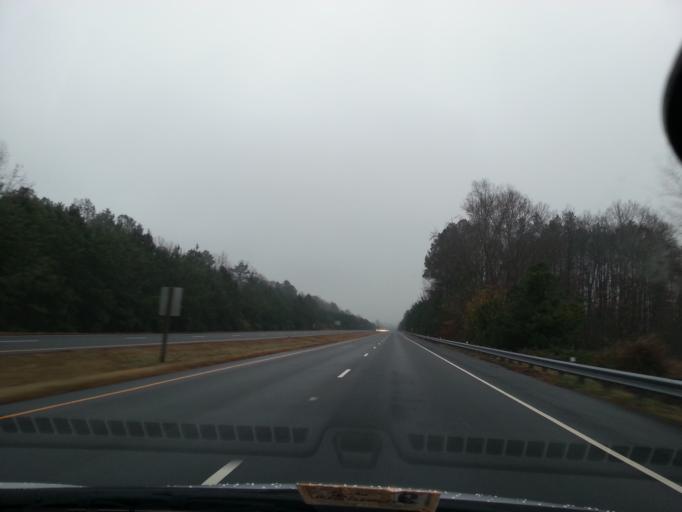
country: US
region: North Carolina
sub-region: Currituck County
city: Moyock
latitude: 36.5979
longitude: -76.1992
